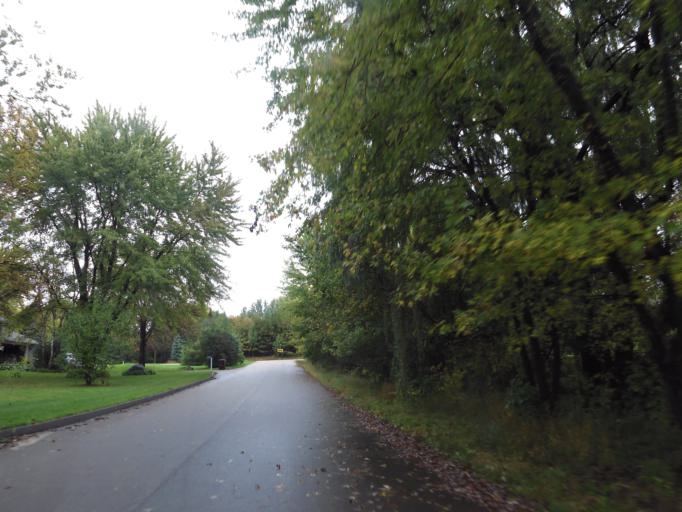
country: US
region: Minnesota
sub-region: Scott County
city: Prior Lake
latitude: 44.6843
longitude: -93.4359
